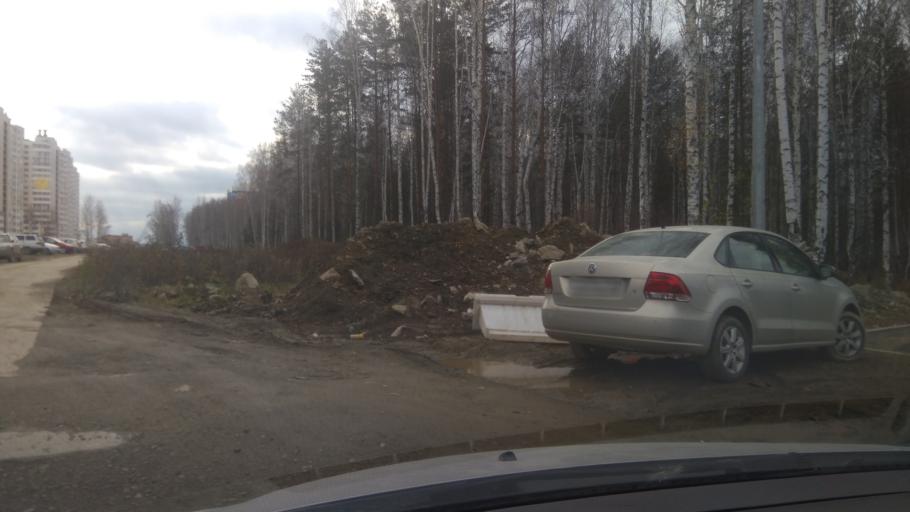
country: RU
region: Sverdlovsk
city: Sovkhoznyy
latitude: 56.7871
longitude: 60.5463
